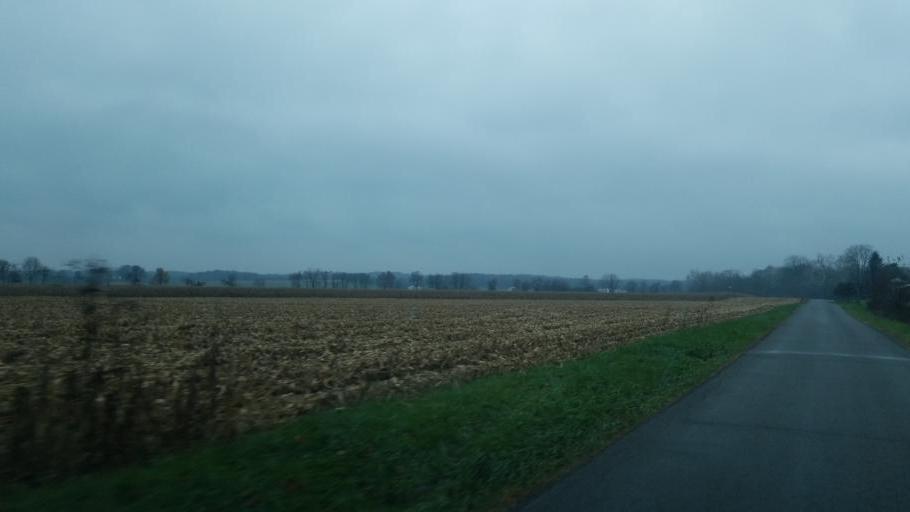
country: US
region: Ohio
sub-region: Knox County
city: Mount Vernon
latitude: 40.4079
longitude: -82.5240
